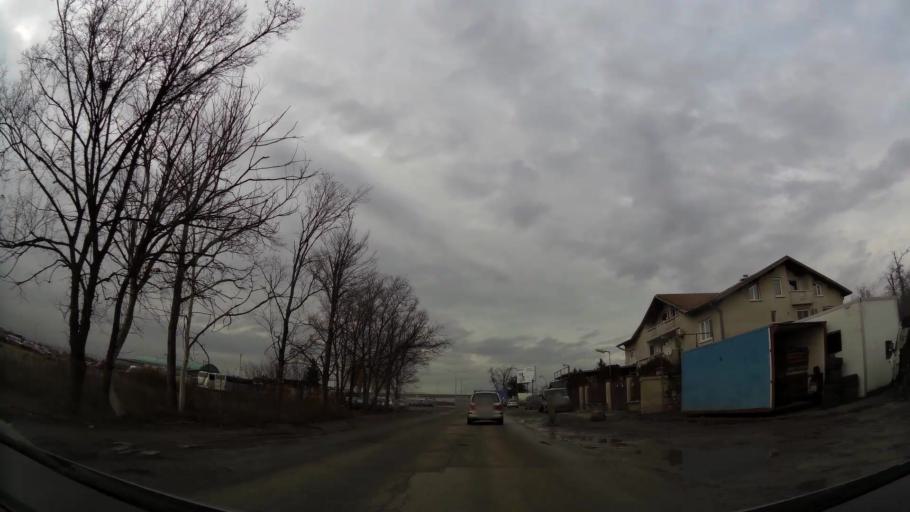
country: BG
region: Sofiya
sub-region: Obshtina Bozhurishte
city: Bozhurishte
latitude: 42.7572
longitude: 23.2697
